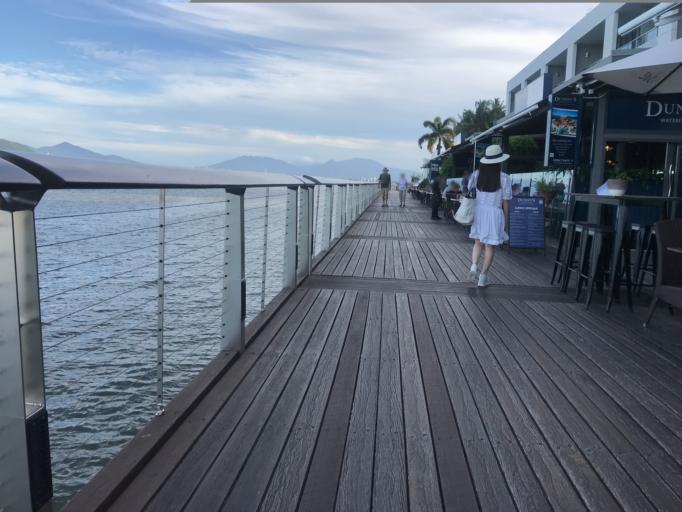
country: AU
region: Queensland
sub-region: Cairns
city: Cairns
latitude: -16.9219
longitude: 145.7809
